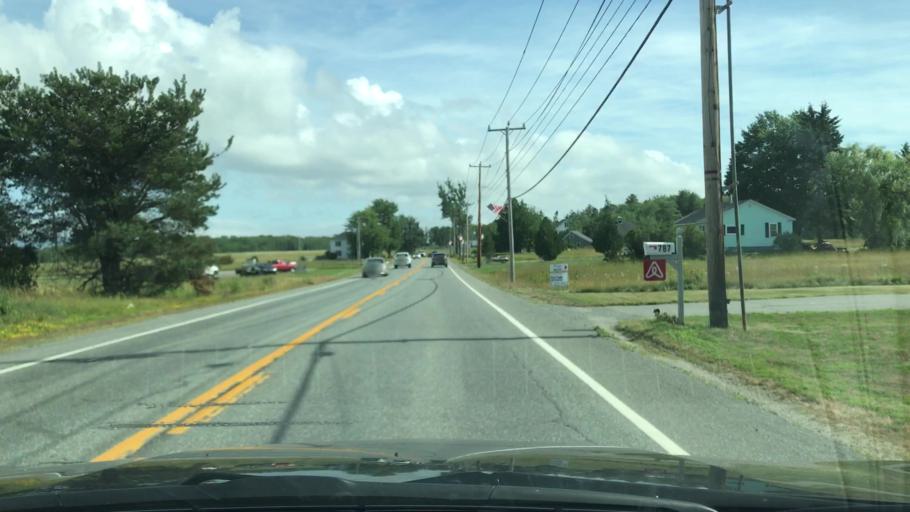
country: US
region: Maine
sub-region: Hancock County
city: Trenton
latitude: 44.4621
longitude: -68.3616
